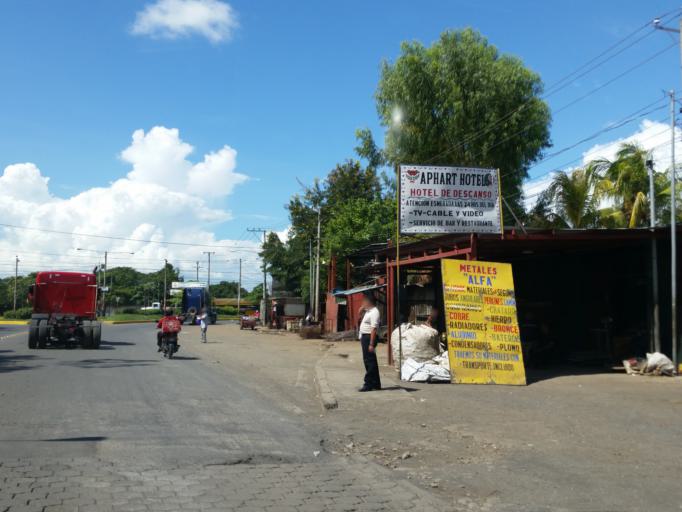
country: NI
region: Managua
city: Managua
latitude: 12.1469
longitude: -86.1952
